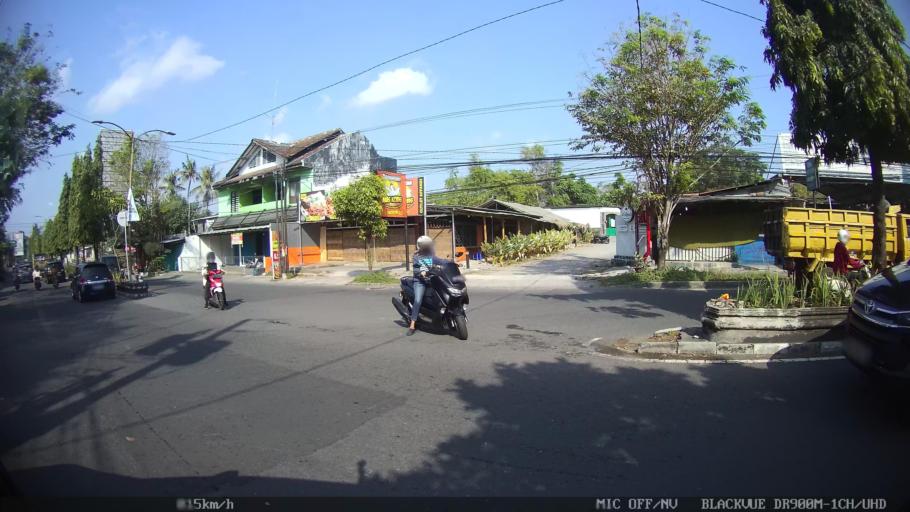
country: ID
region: Daerah Istimewa Yogyakarta
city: Depok
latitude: -7.7616
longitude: 110.3938
